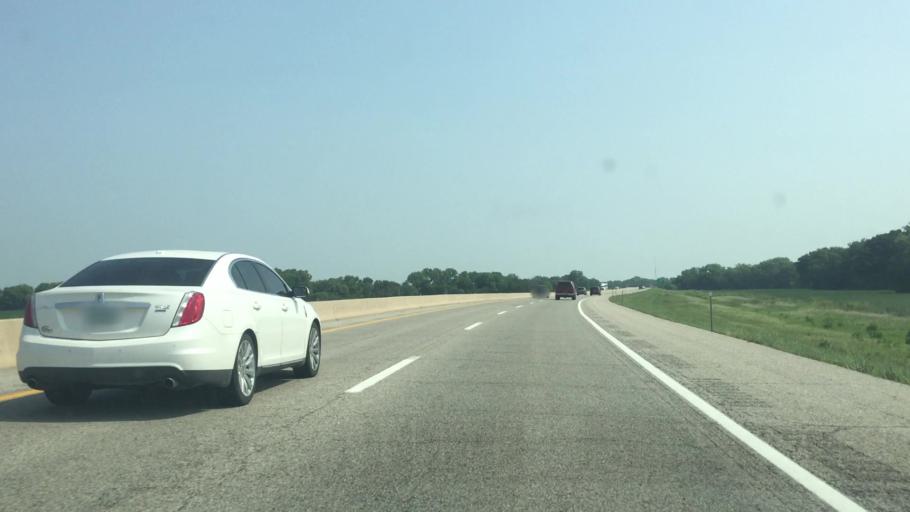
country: US
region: Kansas
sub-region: Lyon County
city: Emporia
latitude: 38.3802
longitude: -96.2654
